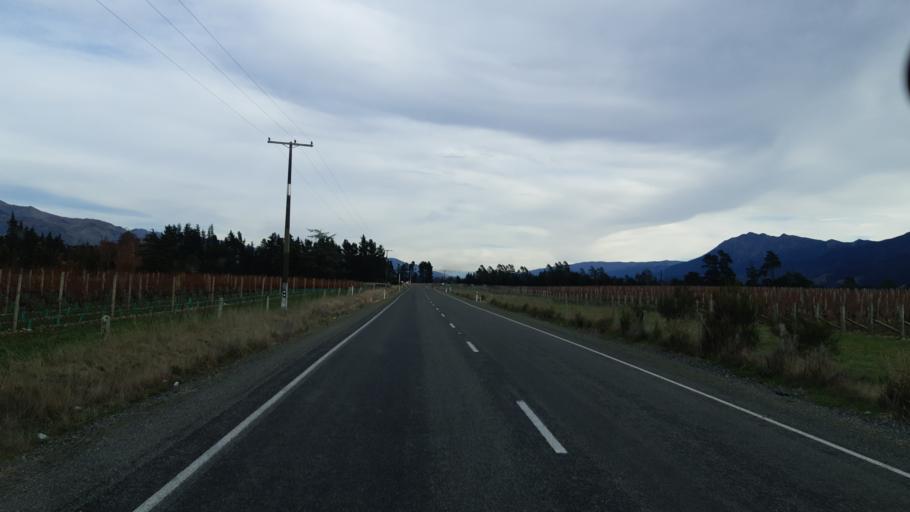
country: NZ
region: Nelson
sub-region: Nelson City
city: Nelson
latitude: -41.6010
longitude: 173.4228
